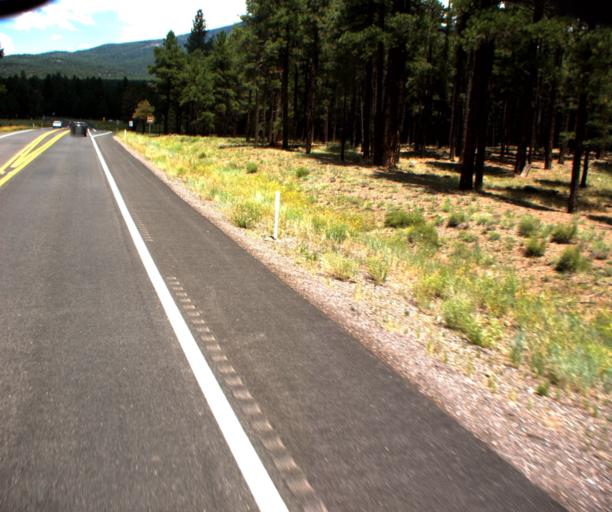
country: US
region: Arizona
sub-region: Coconino County
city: Flagstaff
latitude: 35.2625
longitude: -111.7050
